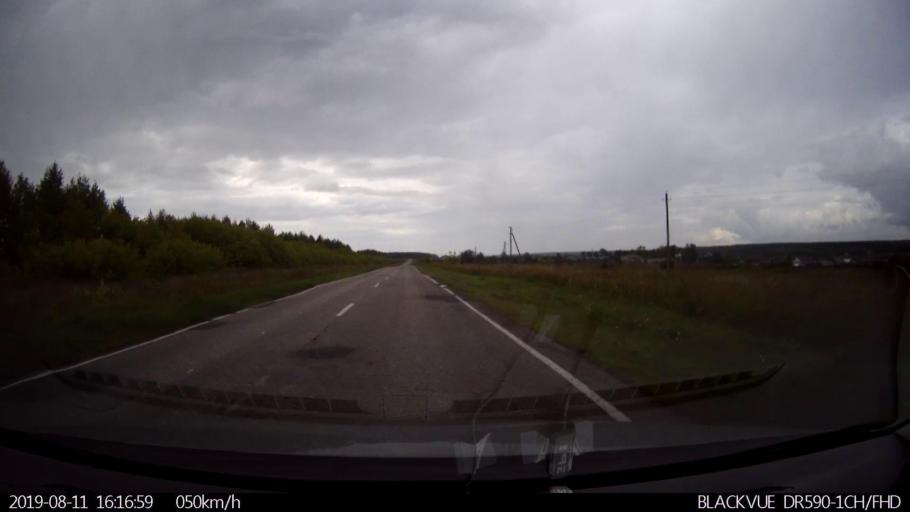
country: RU
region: Ulyanovsk
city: Mayna
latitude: 54.0448
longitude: 47.6188
